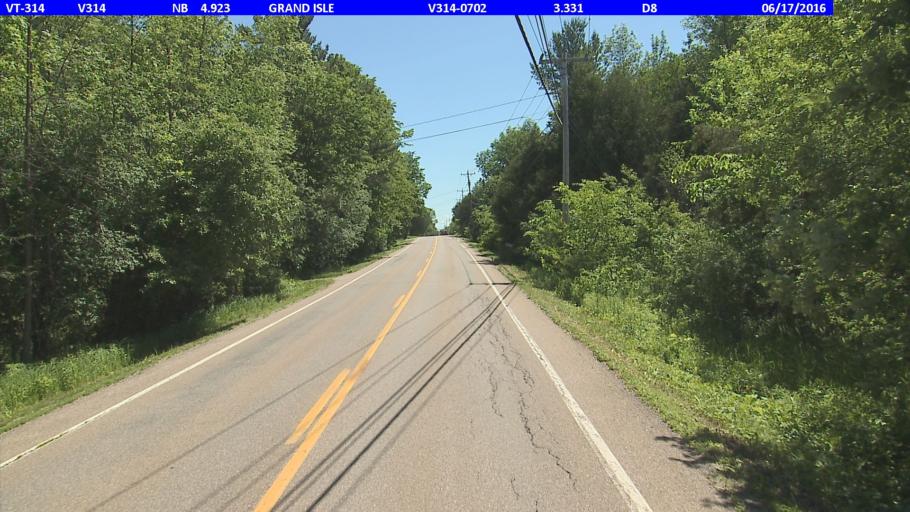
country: US
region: New York
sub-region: Clinton County
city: Cumberland Head
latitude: 44.7021
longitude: -73.3140
